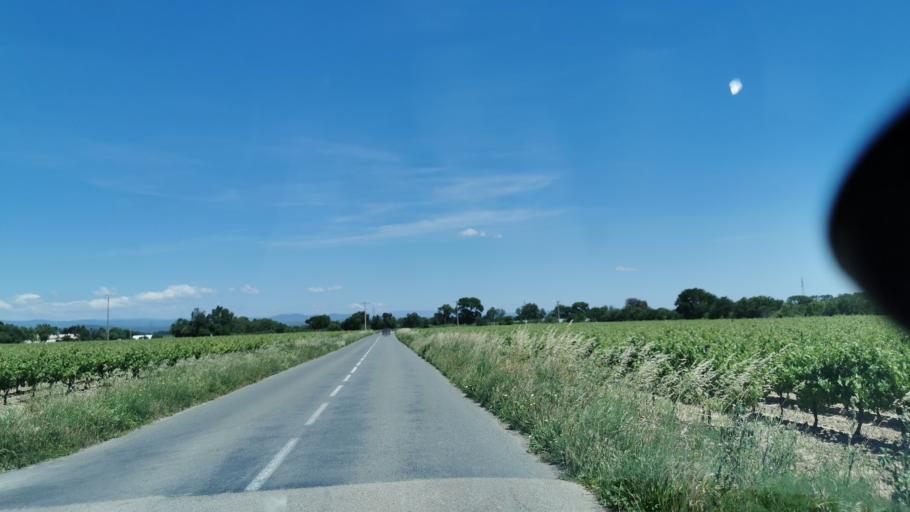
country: FR
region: Languedoc-Roussillon
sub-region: Departement de l'Aude
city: Saint-Marcel-sur-Aude
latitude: 43.2493
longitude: 2.9292
